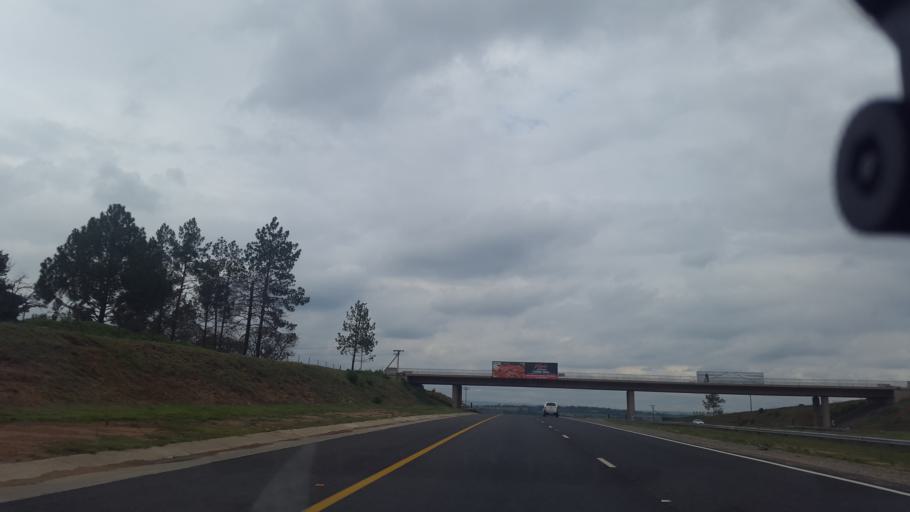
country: ZA
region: Gauteng
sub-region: West Rand District Municipality
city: Muldersdriseloop
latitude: -26.0127
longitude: 27.8793
